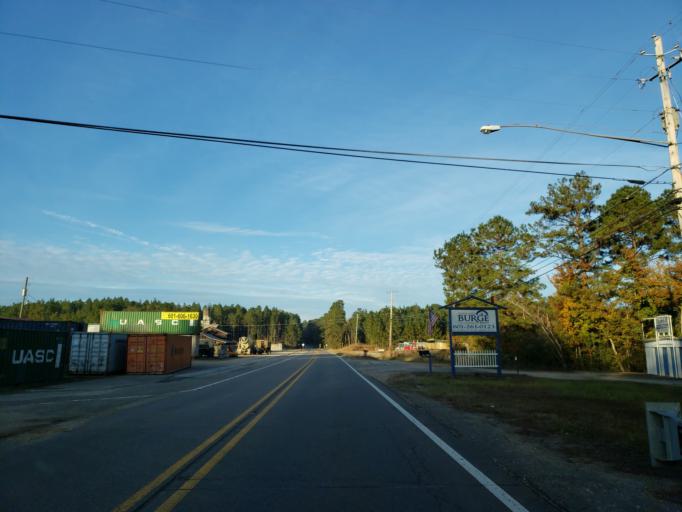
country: US
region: Mississippi
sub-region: Lamar County
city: Purvis
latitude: 31.1501
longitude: -89.4003
